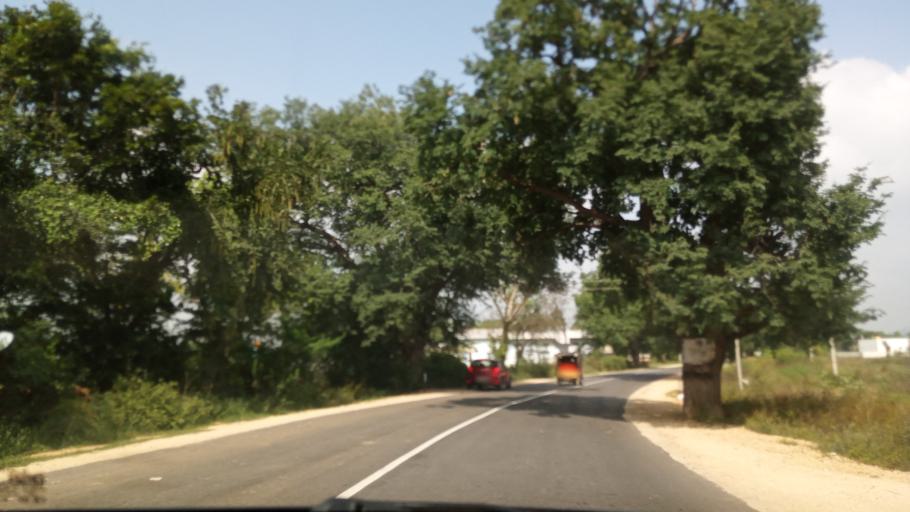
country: IN
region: Andhra Pradesh
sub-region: Chittoor
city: Madanapalle
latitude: 13.6103
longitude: 78.5375
